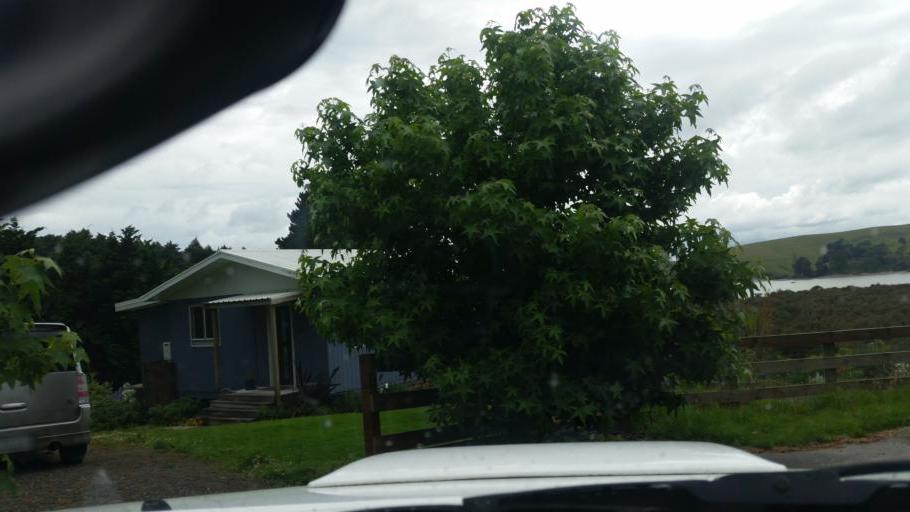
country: NZ
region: Auckland
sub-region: Auckland
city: Wellsford
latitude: -36.1524
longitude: 174.2234
